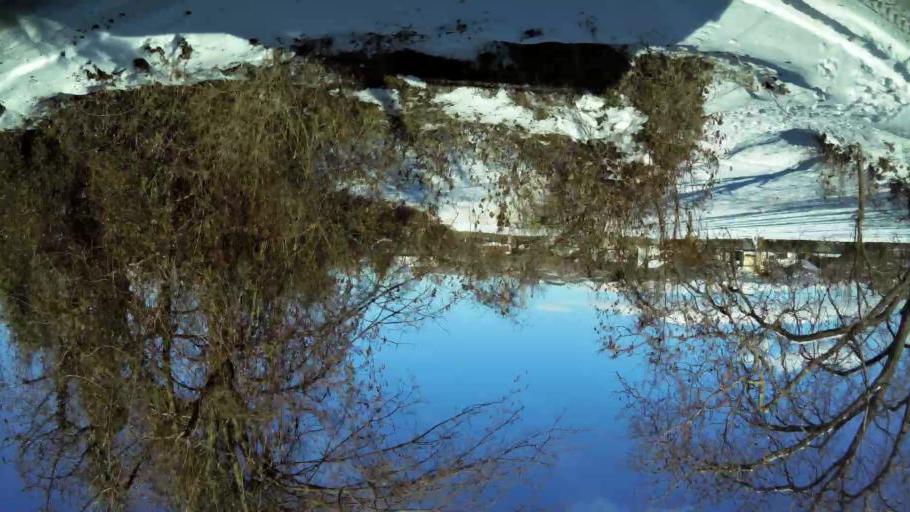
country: MK
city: Grchec
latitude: 41.9777
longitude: 21.3147
